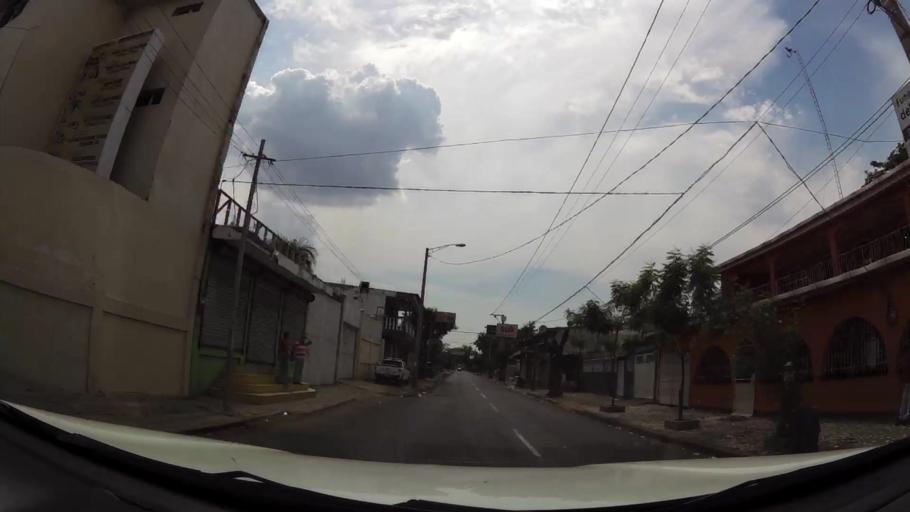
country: NI
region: Managua
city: Managua
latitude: 12.1461
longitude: -86.2779
